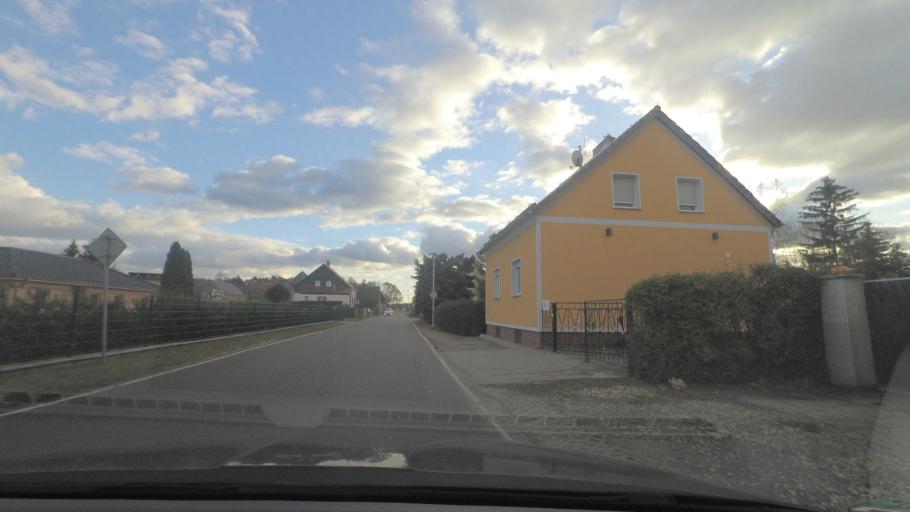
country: DE
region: Brandenburg
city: Sperenberg
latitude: 52.0810
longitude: 13.3215
